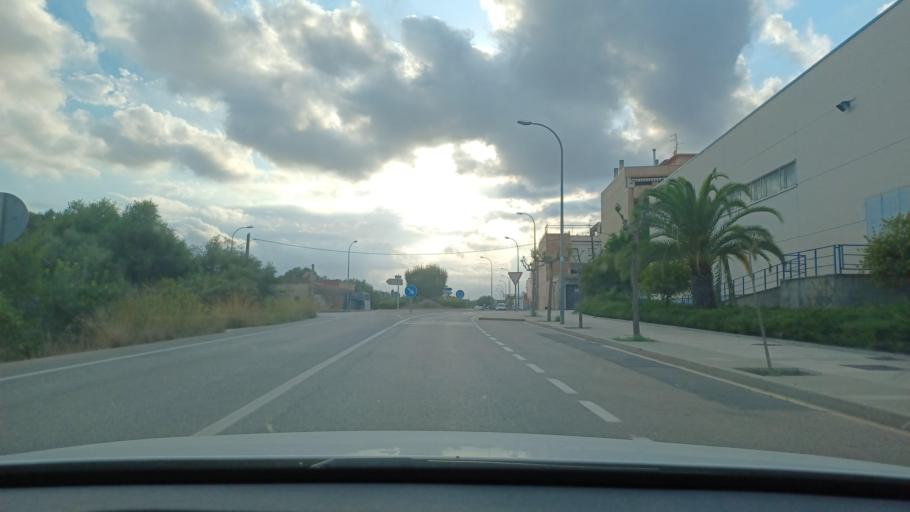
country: ES
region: Catalonia
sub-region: Provincia de Tarragona
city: Alcanar
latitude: 40.5393
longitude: 0.4825
